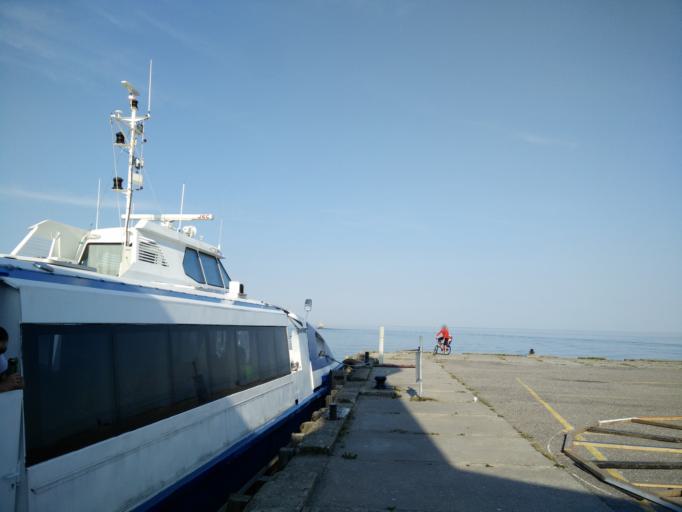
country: LT
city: Nida
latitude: 55.3028
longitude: 21.0100
